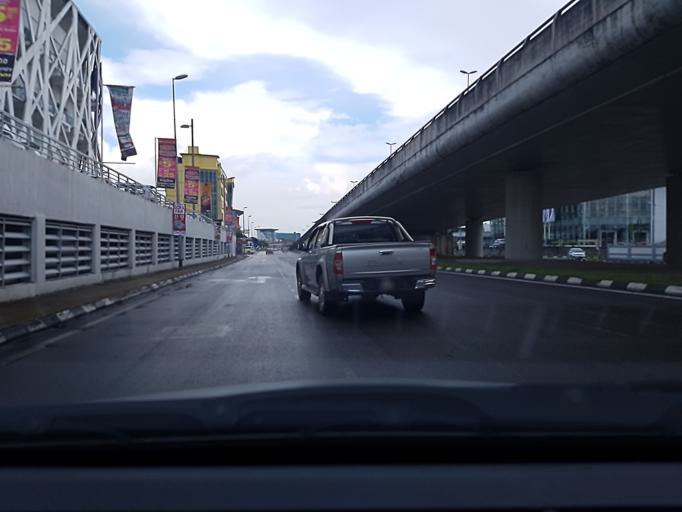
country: MY
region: Sarawak
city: Kuching
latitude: 1.5206
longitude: 110.3542
